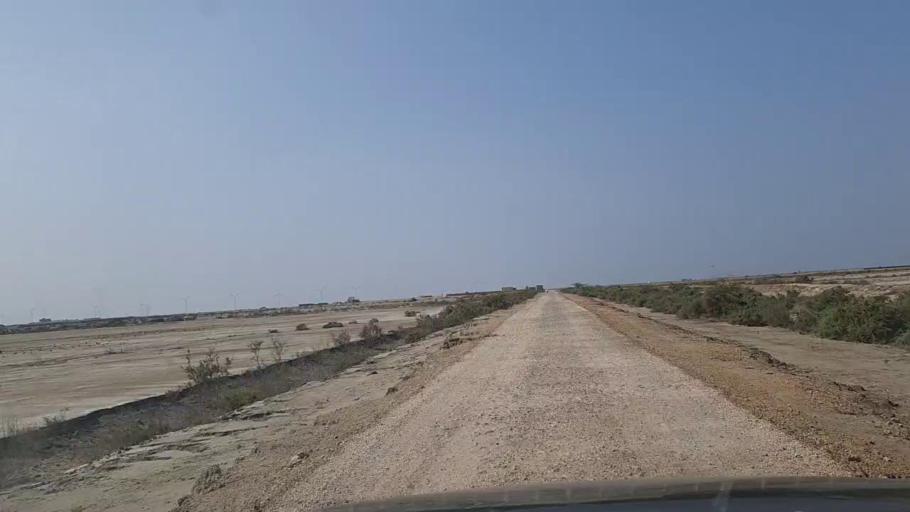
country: PK
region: Sindh
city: Gharo
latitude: 24.7074
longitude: 67.5397
